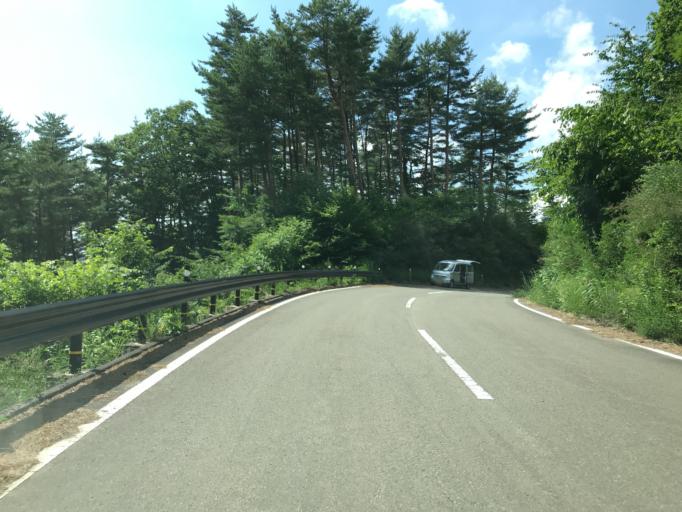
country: JP
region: Fukushima
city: Yanagawamachi-saiwaicho
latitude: 37.7631
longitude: 140.6777
